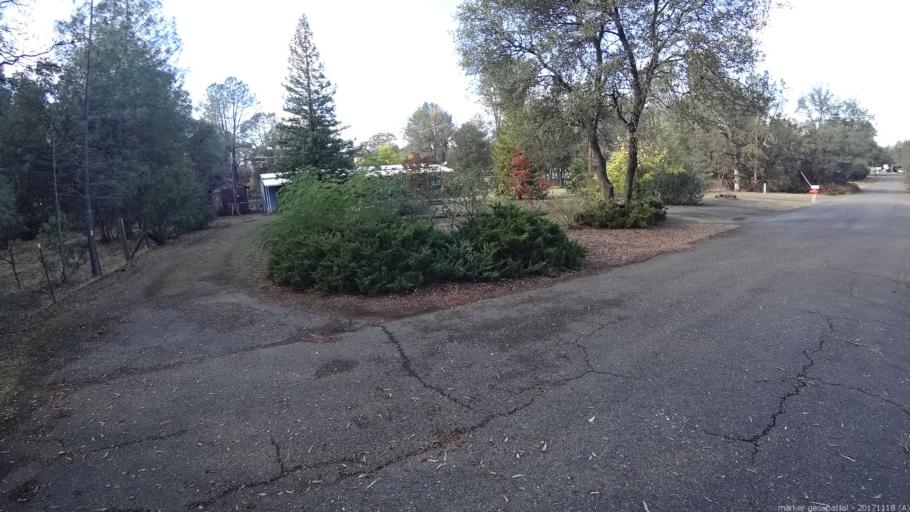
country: US
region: California
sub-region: Shasta County
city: Anderson
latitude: 40.4708
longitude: -122.4131
